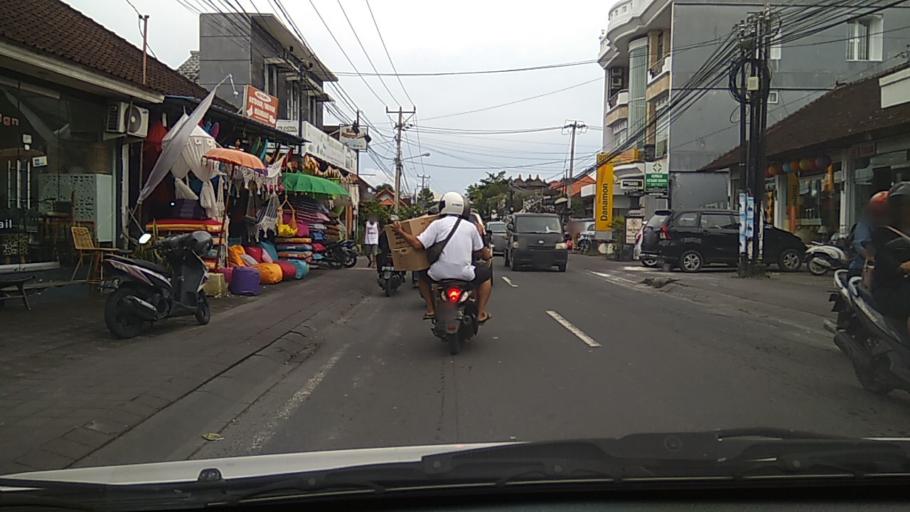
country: ID
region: Bali
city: Kuta
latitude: -8.6740
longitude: 115.1649
